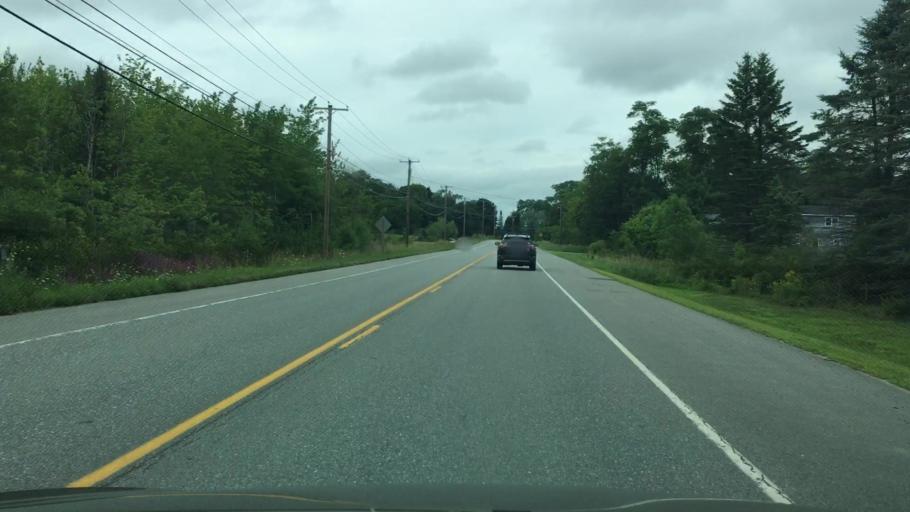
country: US
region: Maine
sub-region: Penobscot County
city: Orrington
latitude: 44.7120
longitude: -68.8262
